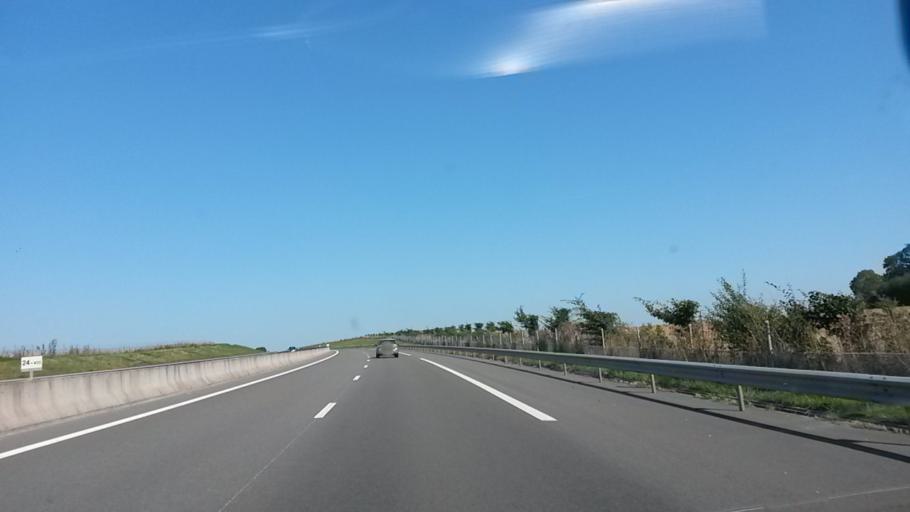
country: FR
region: Nord-Pas-de-Calais
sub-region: Departement du Nord
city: Louvroil
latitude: 50.2350
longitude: 3.9621
